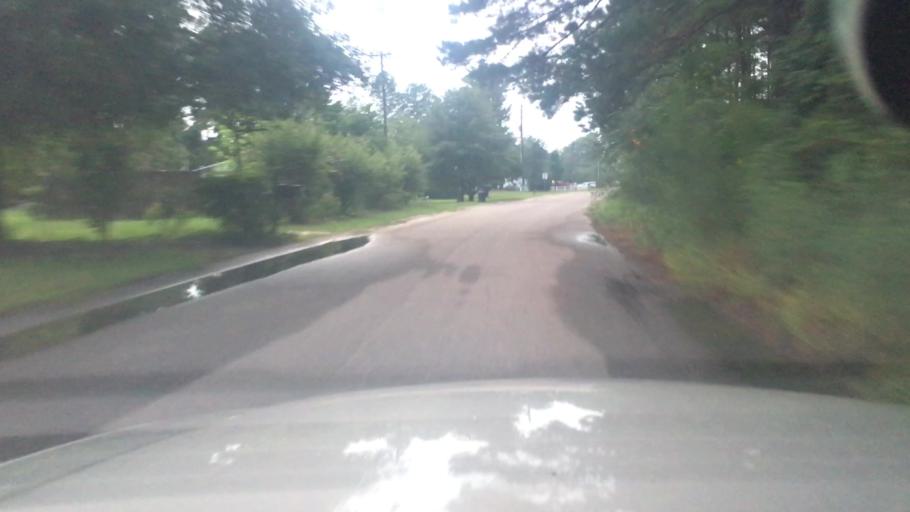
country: US
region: North Carolina
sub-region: Cumberland County
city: Hope Mills
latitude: 34.9622
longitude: -78.9368
